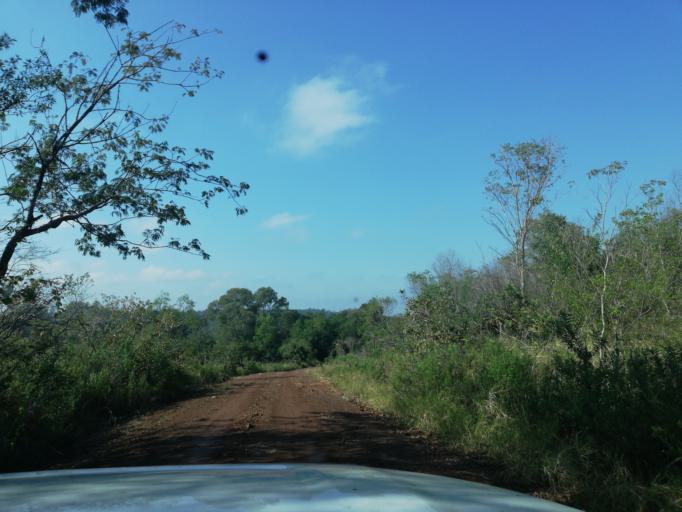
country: AR
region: Misiones
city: Cerro Azul
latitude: -27.6219
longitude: -55.5272
